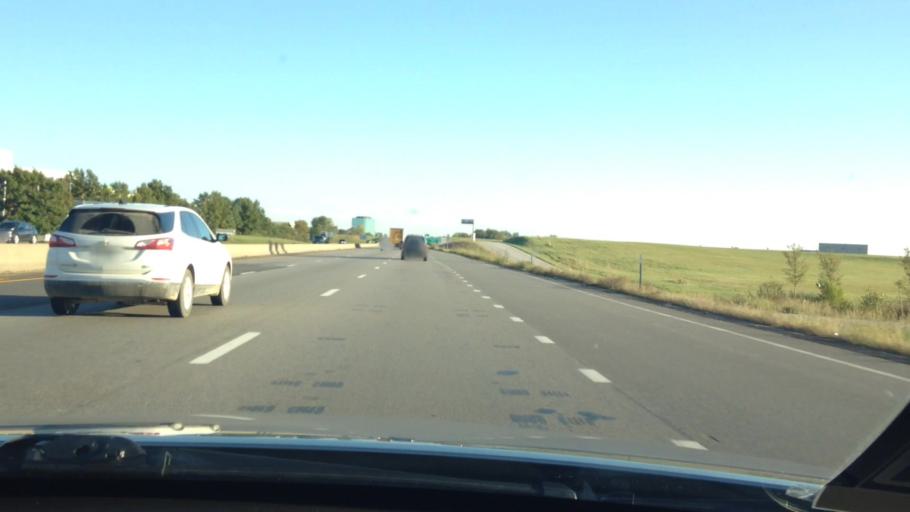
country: US
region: Missouri
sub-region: Platte County
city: Weatherby Lake
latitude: 39.2924
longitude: -94.6835
